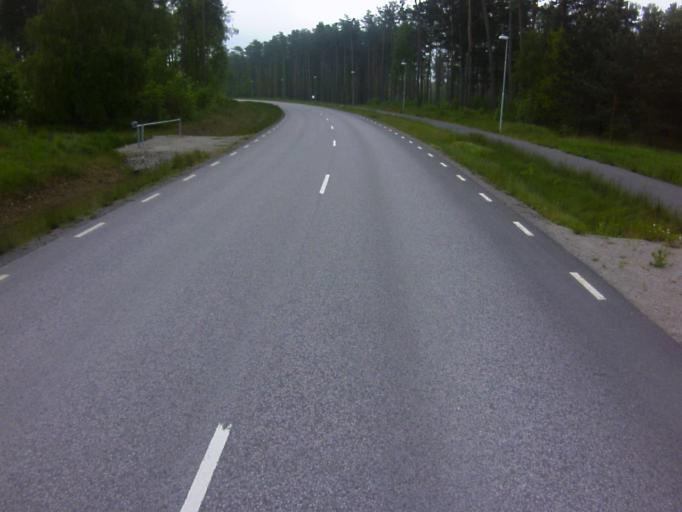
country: SE
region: Blekinge
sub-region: Solvesborgs Kommun
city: Soelvesborg
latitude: 56.0465
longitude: 14.6091
